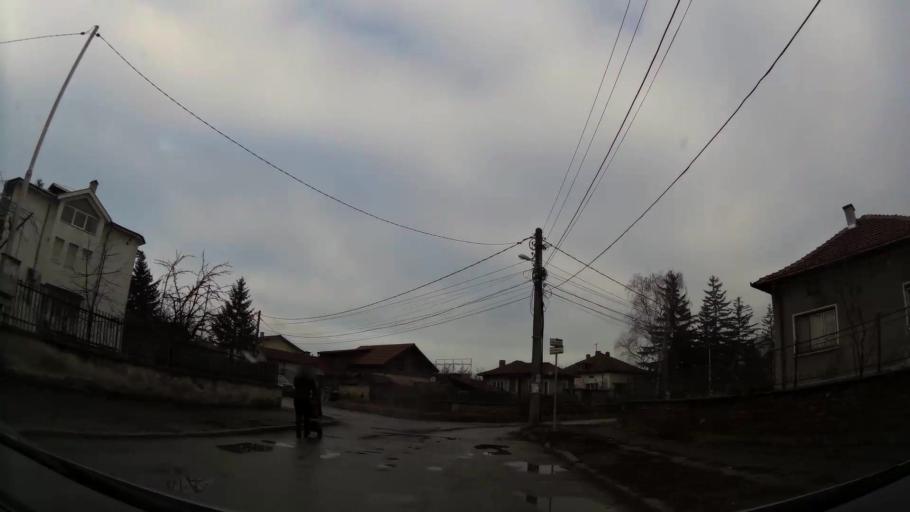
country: BG
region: Sofia-Capital
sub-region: Stolichna Obshtina
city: Sofia
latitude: 42.7392
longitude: 23.3420
